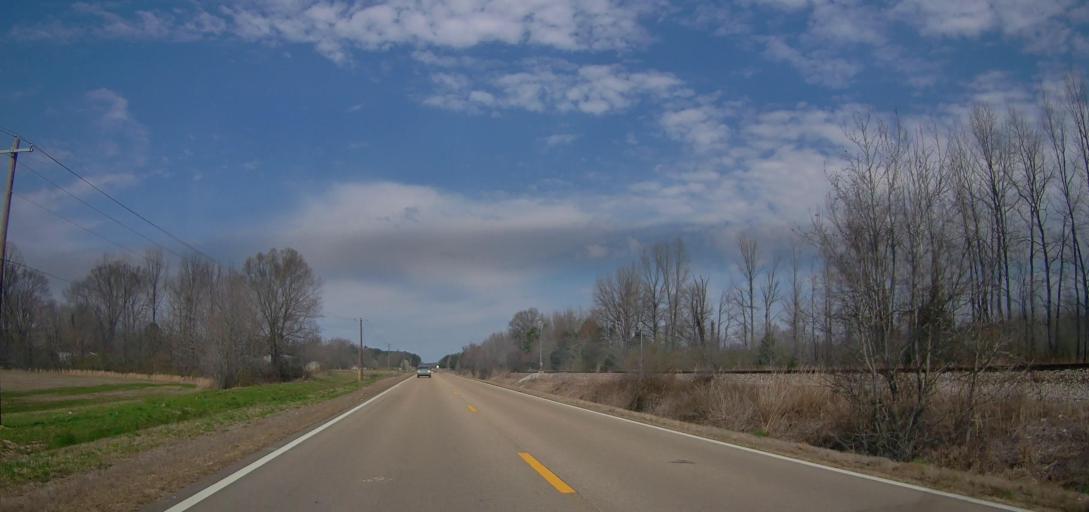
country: US
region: Mississippi
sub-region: Union County
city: New Albany
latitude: 34.5754
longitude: -89.1294
